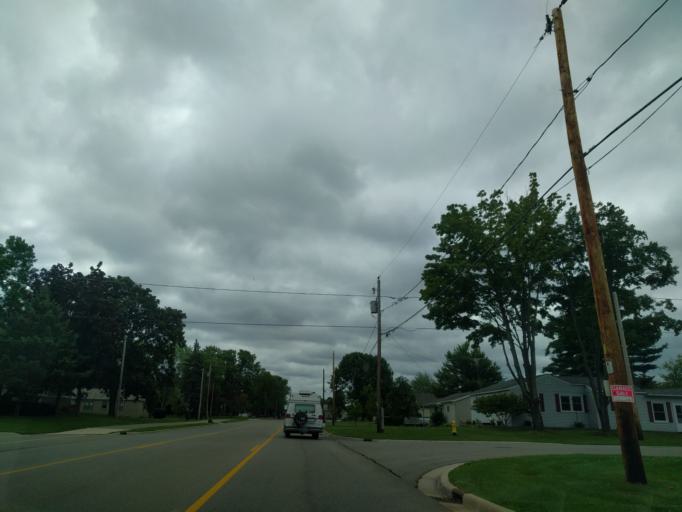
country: US
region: Michigan
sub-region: Menominee County
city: Menominee
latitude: 45.1423
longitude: -87.6034
